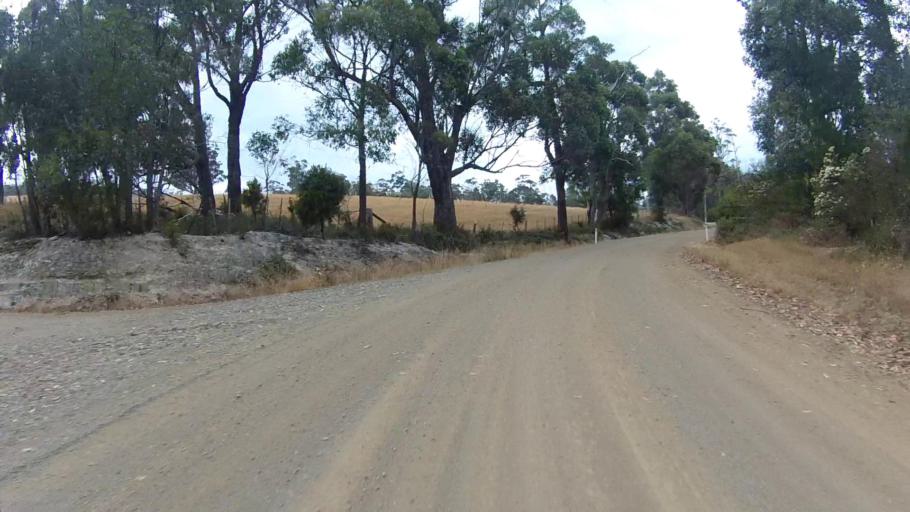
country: AU
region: Tasmania
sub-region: Huon Valley
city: Cygnet
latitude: -43.2311
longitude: 147.0992
